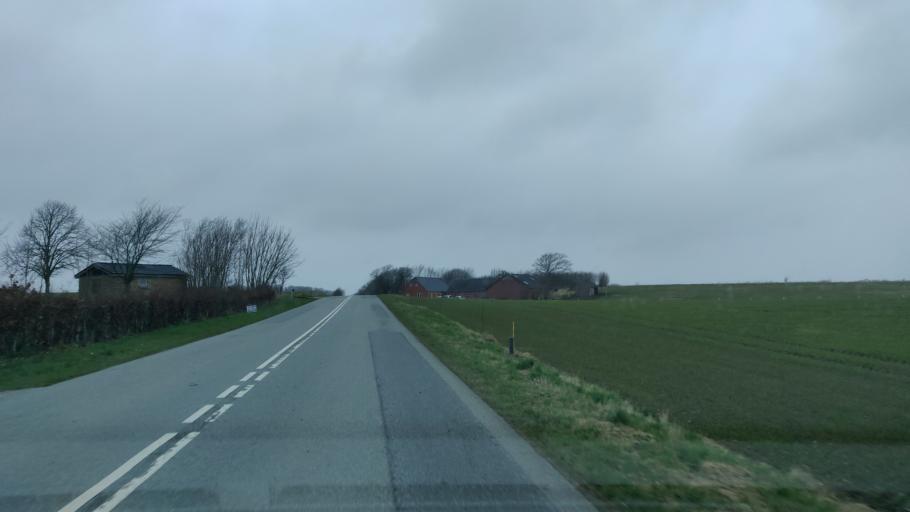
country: DK
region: Central Jutland
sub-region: Skive Kommune
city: Hojslev
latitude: 56.5870
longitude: 9.2241
